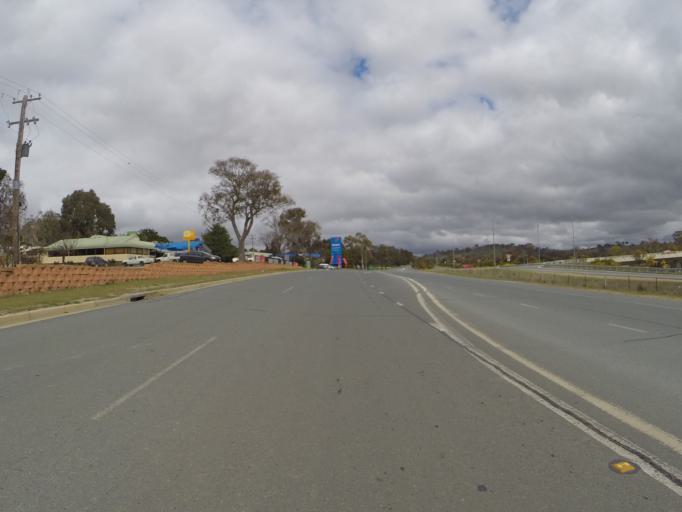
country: AU
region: Australian Capital Territory
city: Kaleen
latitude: -35.2021
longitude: 149.2120
